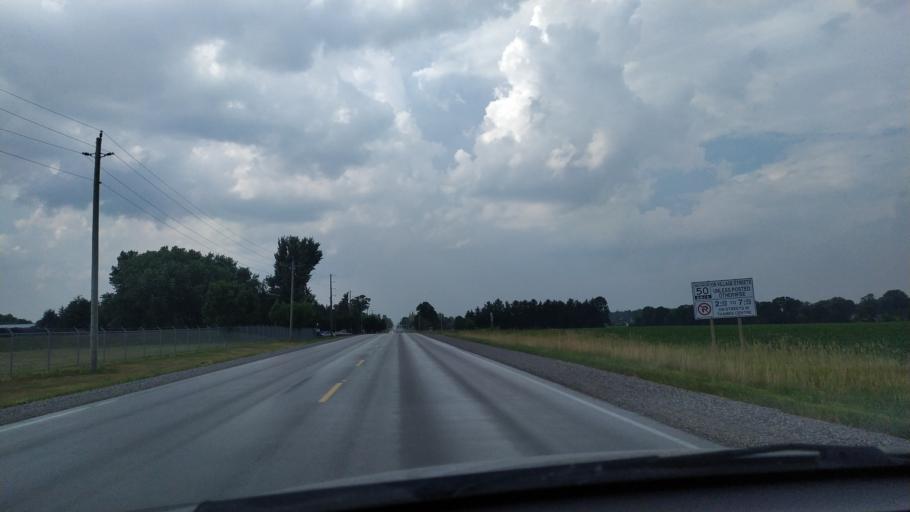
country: CA
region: Ontario
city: London
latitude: 43.0958
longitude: -81.1537
